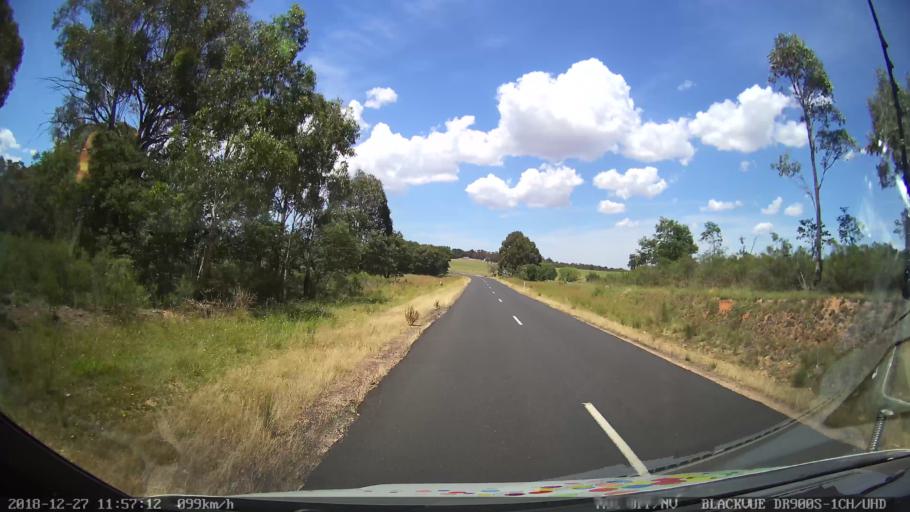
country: AU
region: New South Wales
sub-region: Blayney
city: Blayney
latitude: -33.7085
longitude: 149.3869
